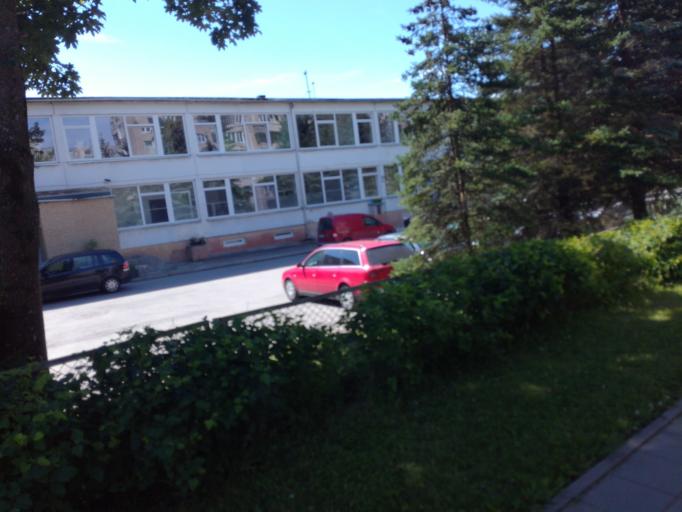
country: LT
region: Alytaus apskritis
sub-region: Alytus
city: Alytus
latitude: 54.3949
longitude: 24.0315
